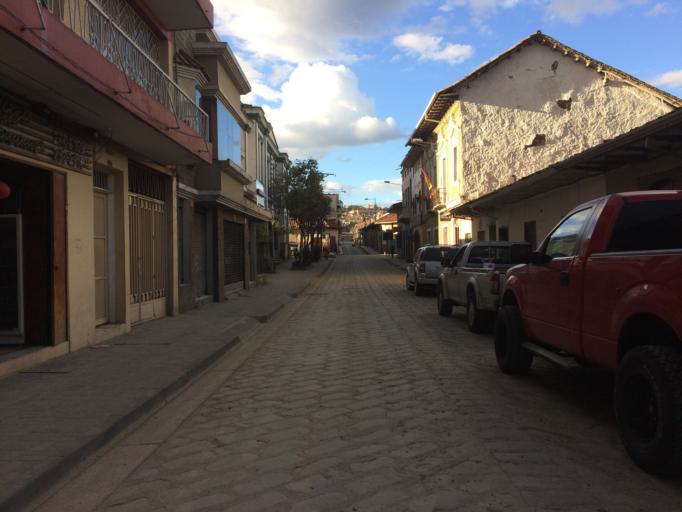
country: EC
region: Azuay
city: Cuenca
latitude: -2.8937
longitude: -79.0073
